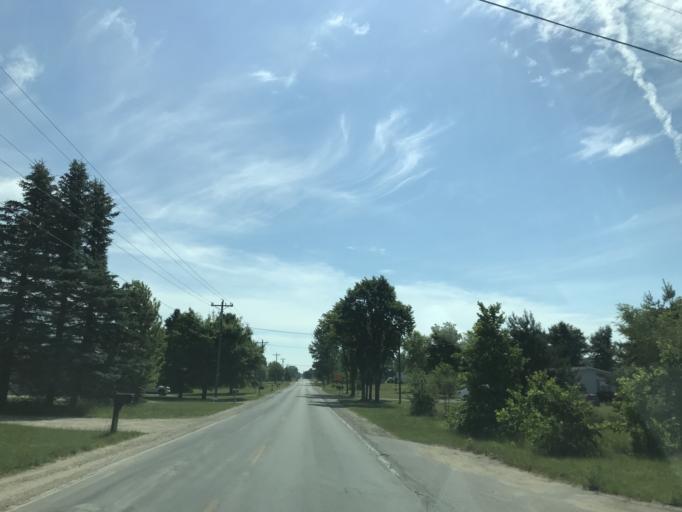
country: US
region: Michigan
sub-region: Grand Traverse County
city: Traverse City
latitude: 44.6576
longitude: -85.6807
